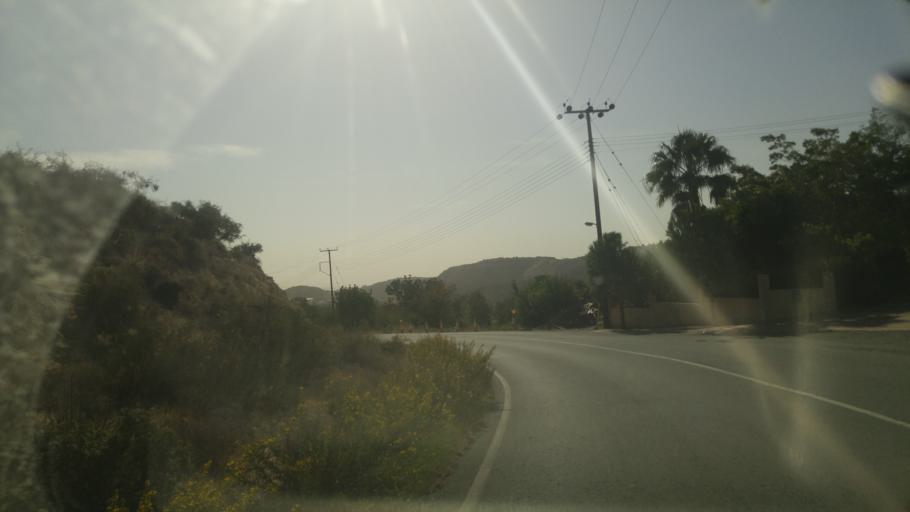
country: CY
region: Limassol
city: Pano Polemidia
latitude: 34.7393
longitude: 33.0254
